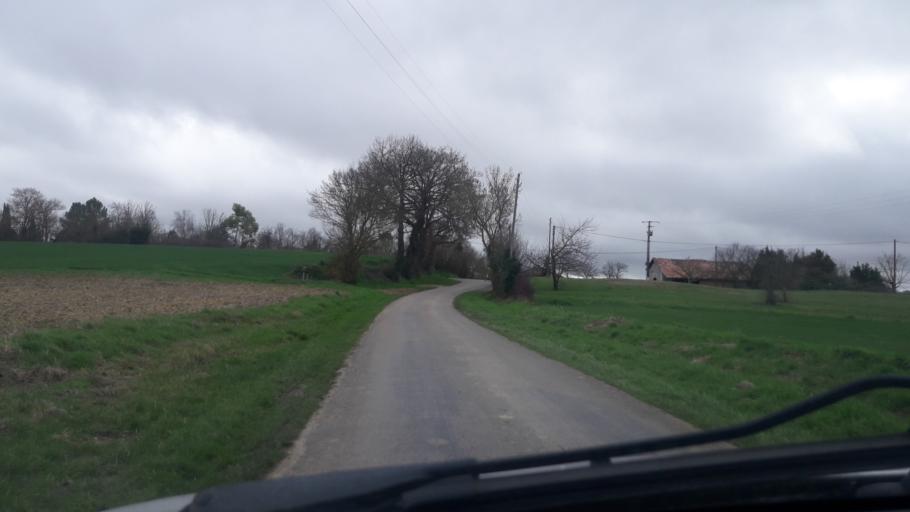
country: FR
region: Midi-Pyrenees
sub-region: Departement du Gers
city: Gimont
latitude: 43.6516
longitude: 0.9658
